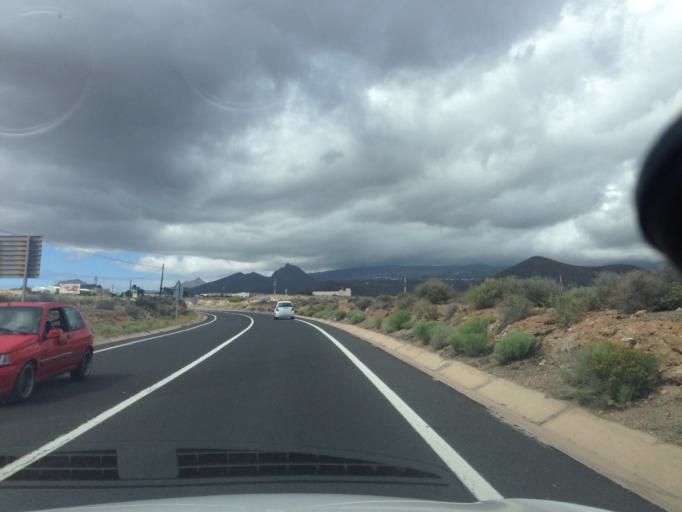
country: ES
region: Canary Islands
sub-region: Provincia de Santa Cruz de Tenerife
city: Las Rosas
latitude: 28.0434
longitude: -16.6062
